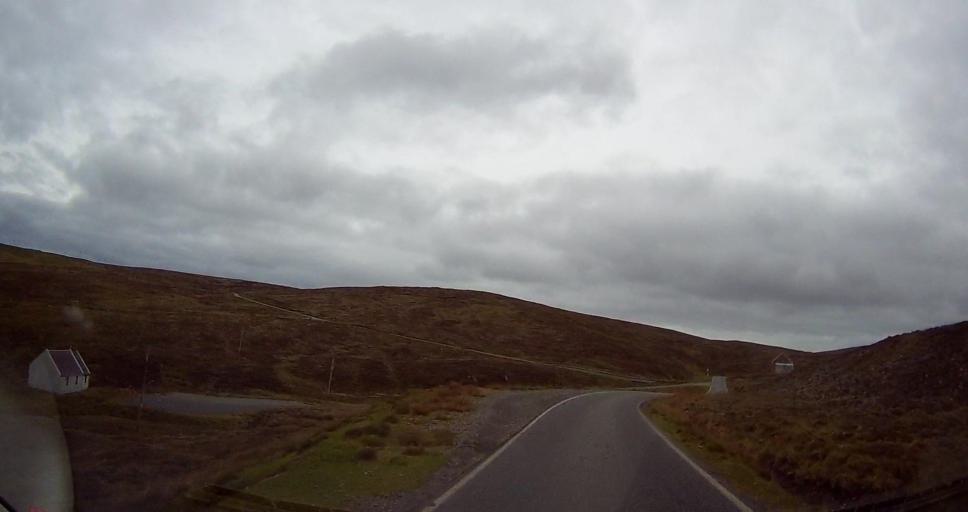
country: GB
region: Scotland
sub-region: Shetland Islands
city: Shetland
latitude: 60.5511
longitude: -1.0603
